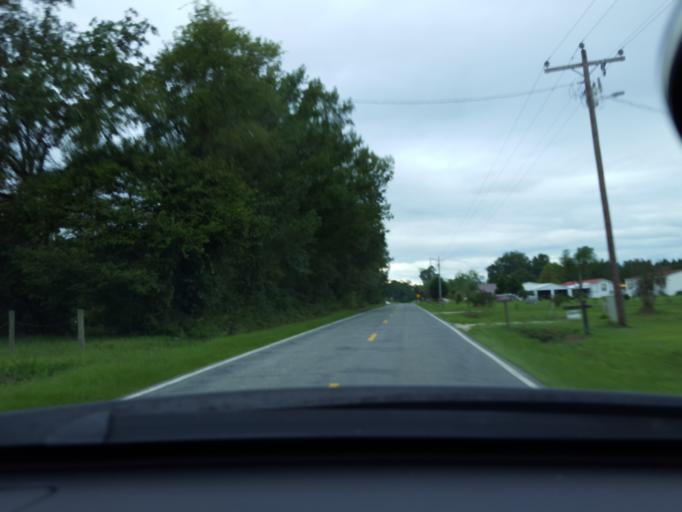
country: US
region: North Carolina
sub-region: Sampson County
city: Clinton
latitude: 34.7781
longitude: -78.3313
